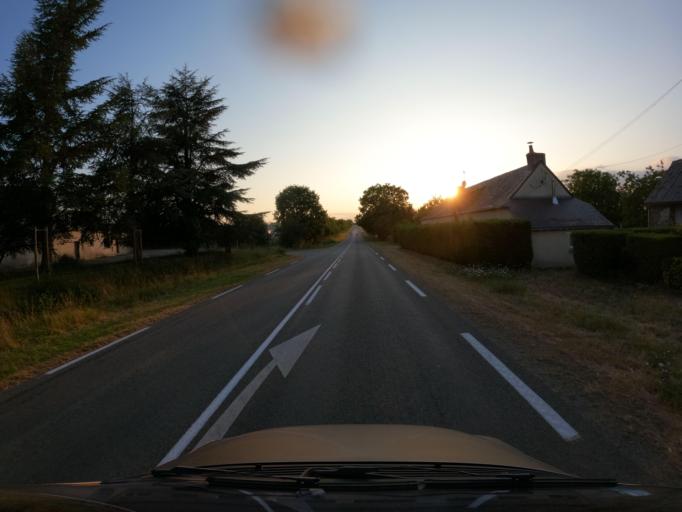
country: FR
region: Pays de la Loire
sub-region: Departement de la Mayenne
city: Meslay-du-Maine
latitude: 47.8724
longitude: -0.5000
